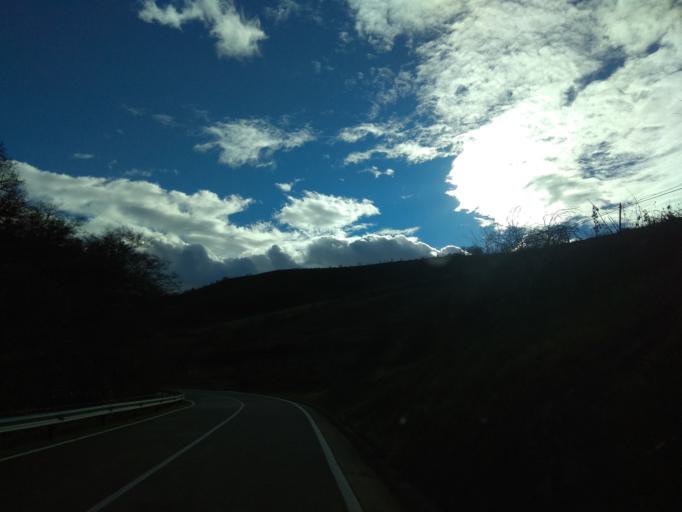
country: ES
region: Cantabria
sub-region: Provincia de Cantabria
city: San Martin de Elines
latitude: 42.8547
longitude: -3.9136
